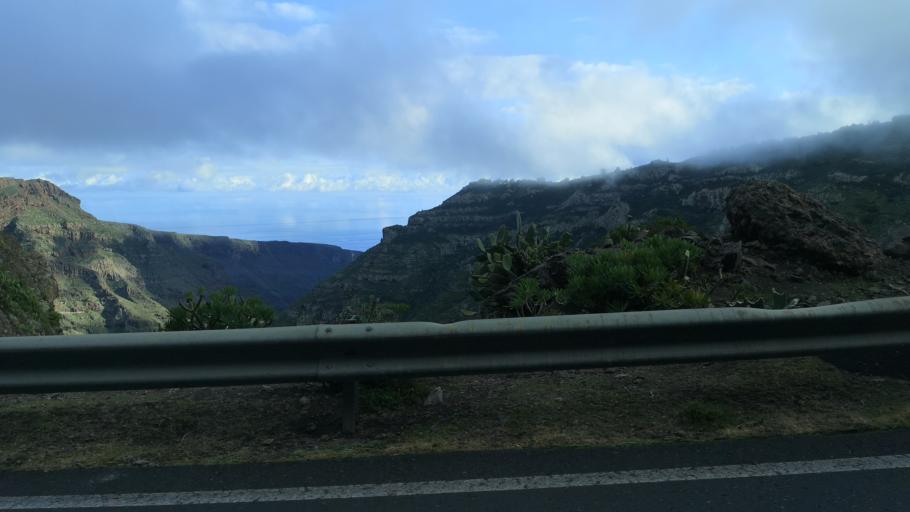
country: ES
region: Canary Islands
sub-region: Provincia de Santa Cruz de Tenerife
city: Alajero
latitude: 28.0936
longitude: -17.1960
